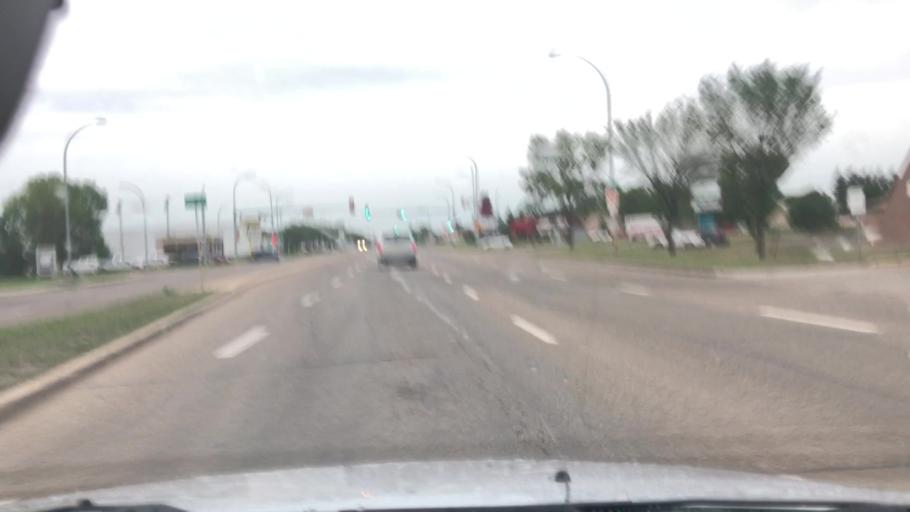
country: CA
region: Alberta
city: St. Albert
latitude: 53.5589
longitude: -113.5921
